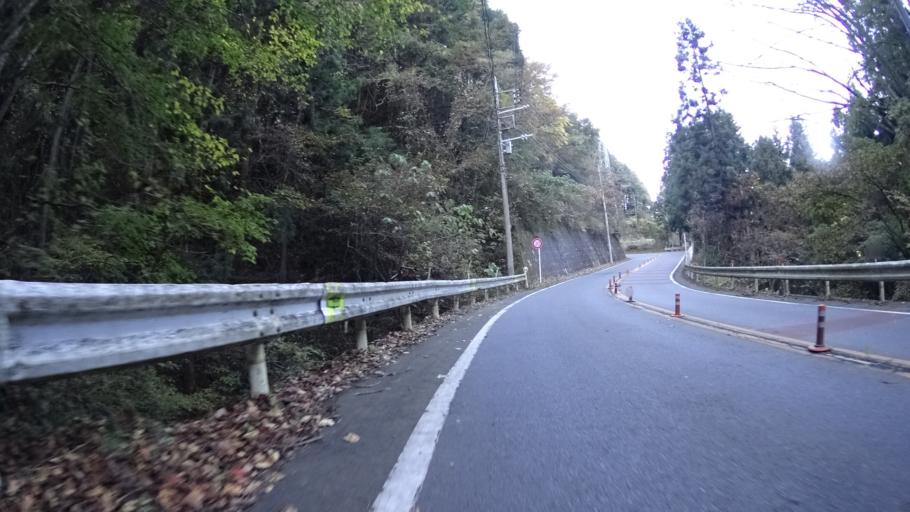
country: JP
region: Yamanashi
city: Uenohara
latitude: 35.6977
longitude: 139.1062
